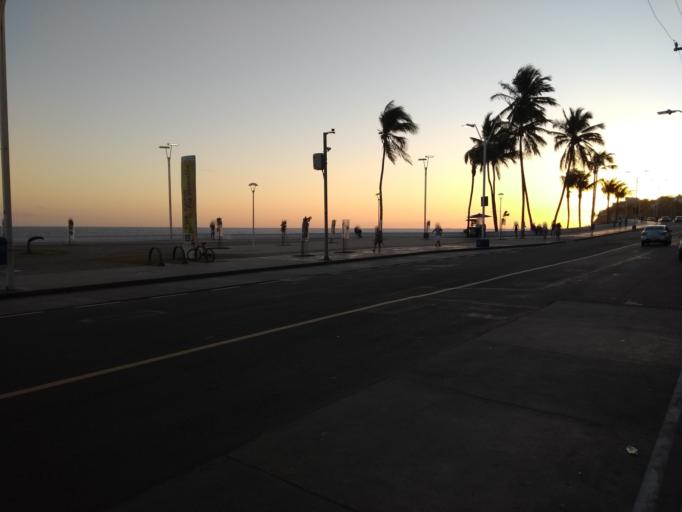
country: BR
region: Bahia
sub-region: Salvador
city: Salvador
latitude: -13.0111
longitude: -38.4936
